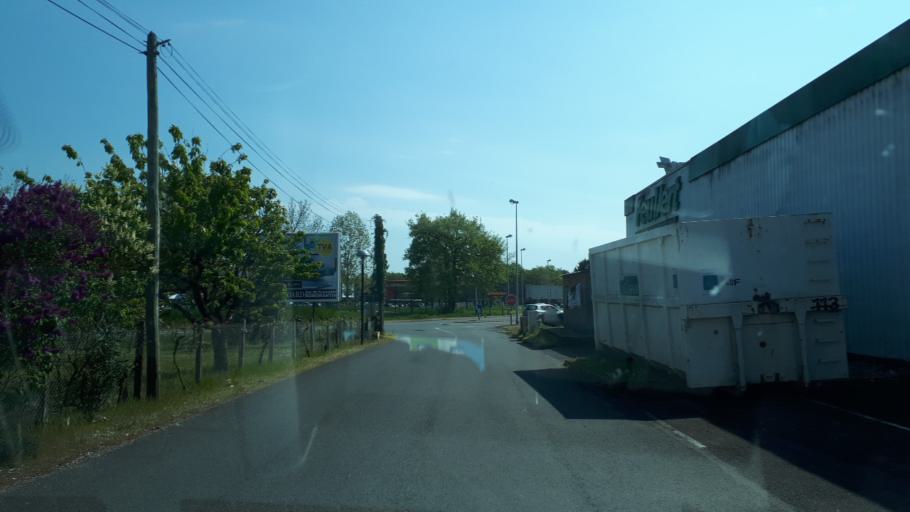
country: FR
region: Centre
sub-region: Departement du Loir-et-Cher
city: Romorantin-Lanthenay
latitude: 47.3775
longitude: 1.7342
